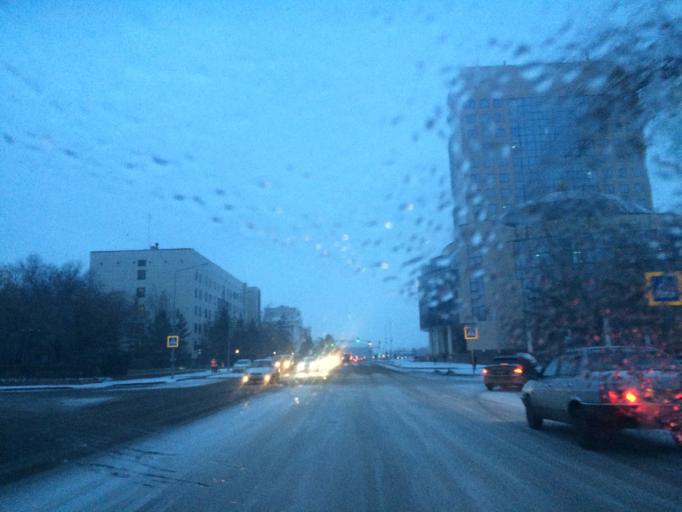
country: KZ
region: Astana Qalasy
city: Astana
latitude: 51.1696
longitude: 71.4203
